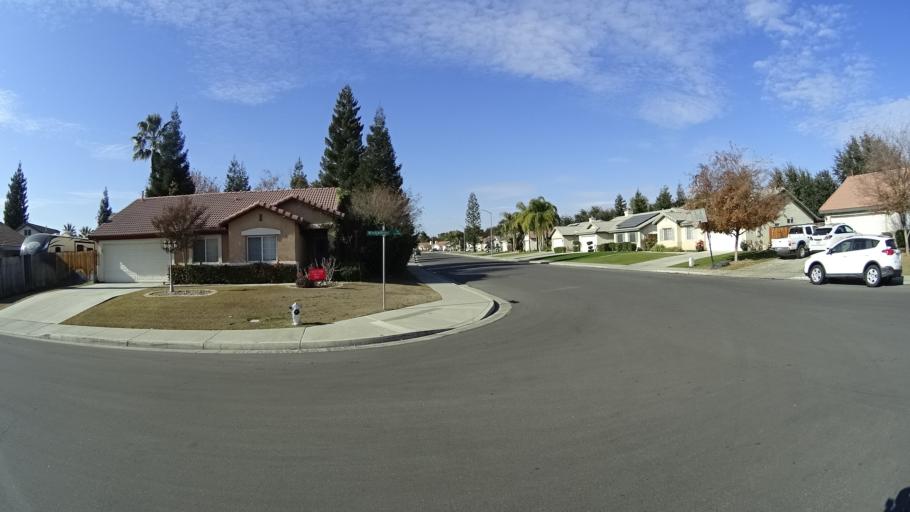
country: US
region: California
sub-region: Kern County
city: Greenacres
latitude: 35.4121
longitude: -119.0958
